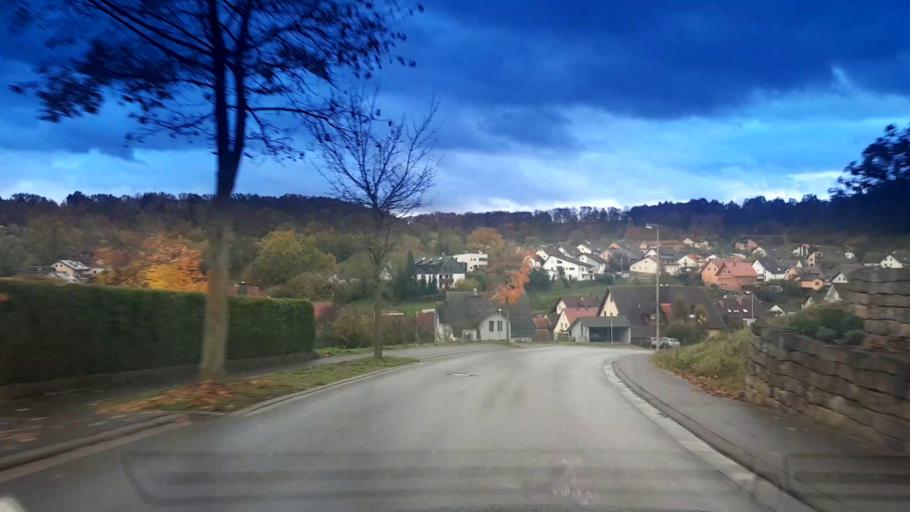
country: DE
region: Bavaria
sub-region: Upper Franconia
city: Viereth-Trunstadt
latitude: 49.9215
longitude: 10.7741
